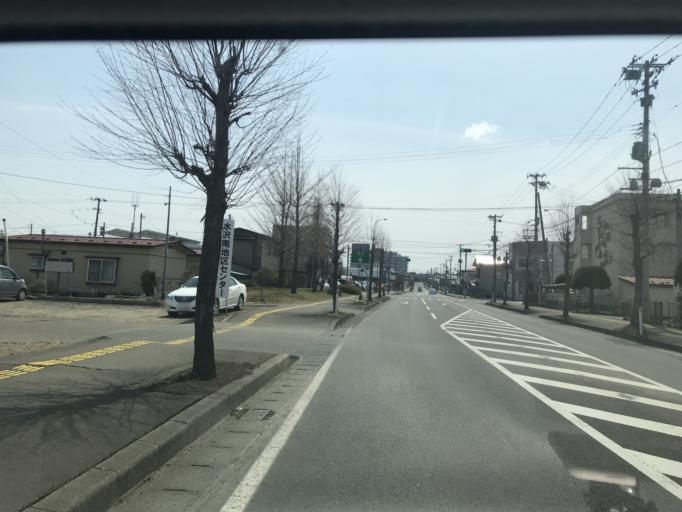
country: JP
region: Iwate
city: Mizusawa
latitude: 39.1295
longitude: 141.1360
